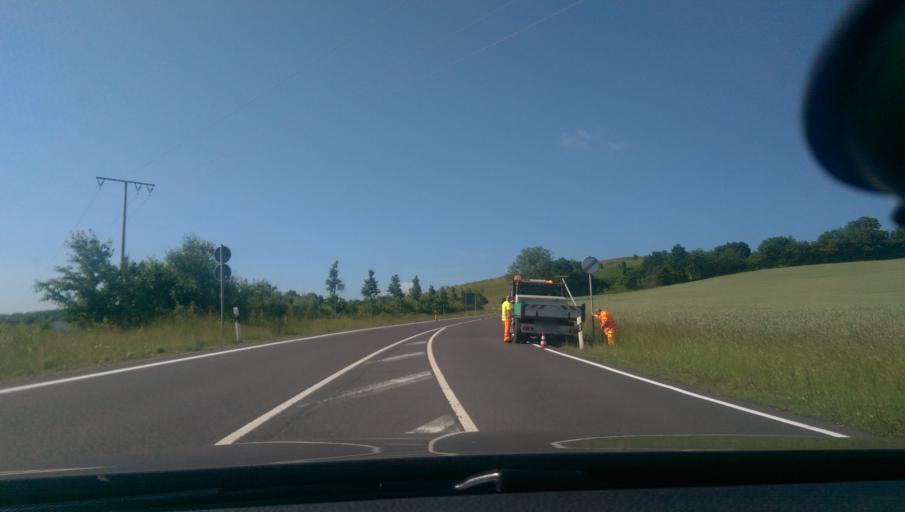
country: DE
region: Thuringia
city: Krauthausen
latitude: 51.0183
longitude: 10.2612
